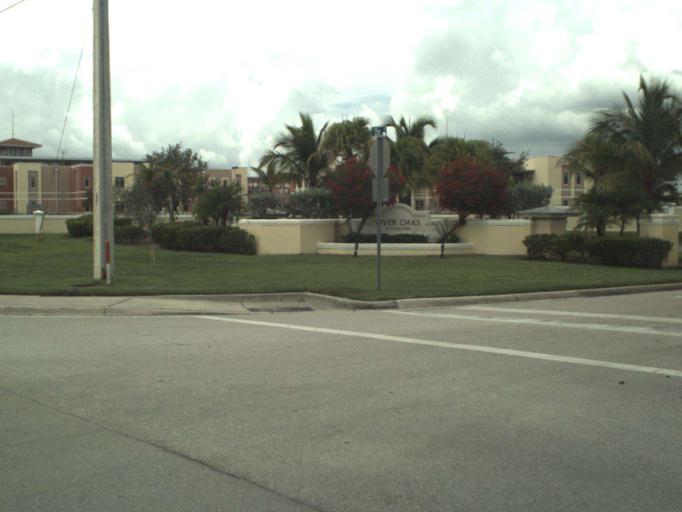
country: US
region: Florida
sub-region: Saint Lucie County
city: Fort Pierce South
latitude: 27.3933
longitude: -80.3501
